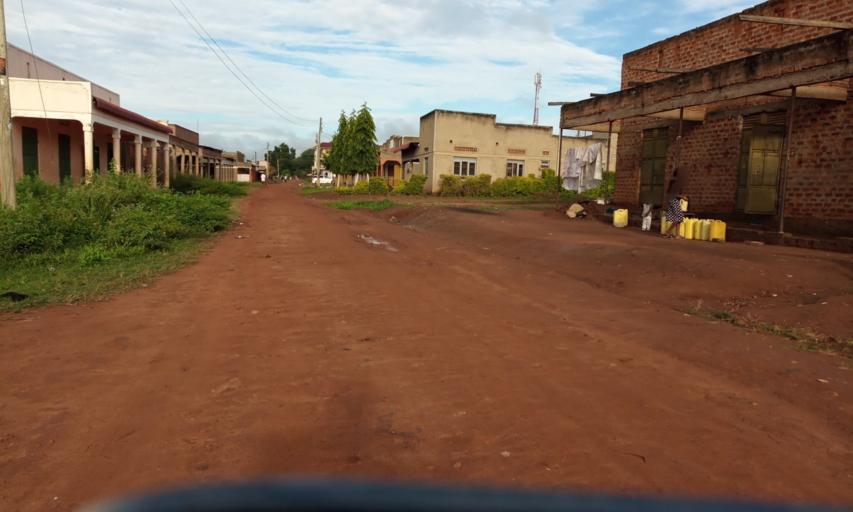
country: UG
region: Eastern Region
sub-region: Mbale District
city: Mbale
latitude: 1.1407
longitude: 34.1670
